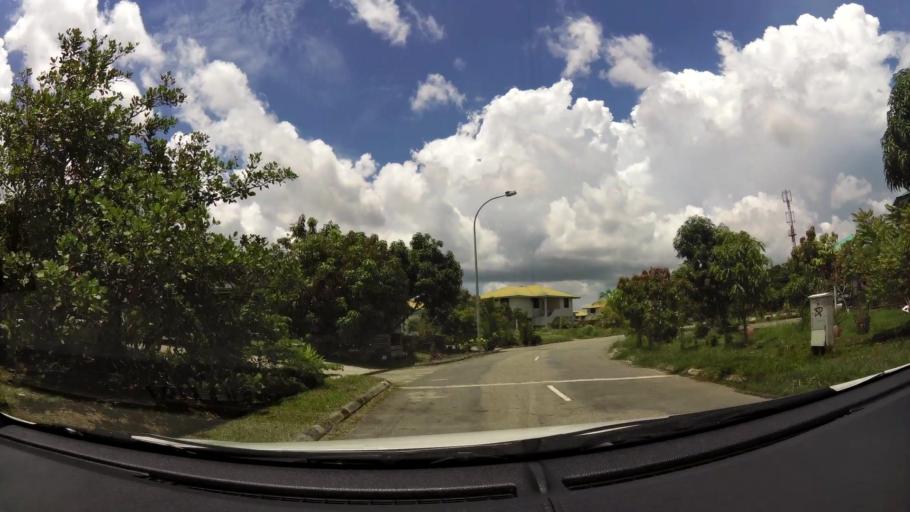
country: BN
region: Brunei and Muara
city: Bandar Seri Begawan
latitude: 4.9607
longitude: 114.9150
